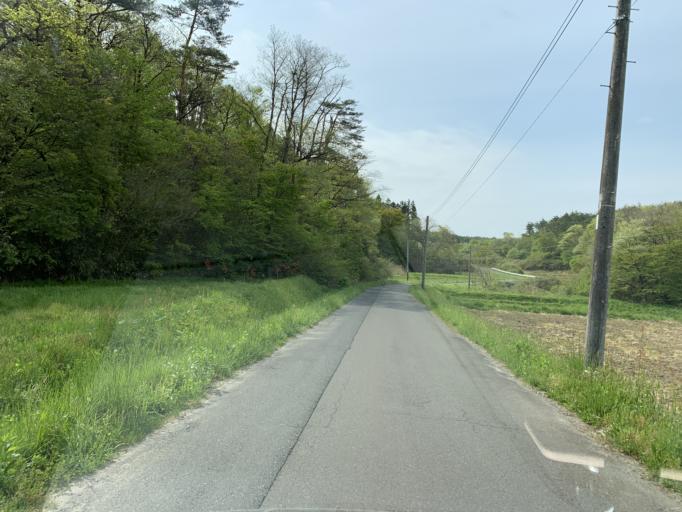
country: JP
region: Iwate
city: Ichinoseki
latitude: 38.9030
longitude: 141.0572
